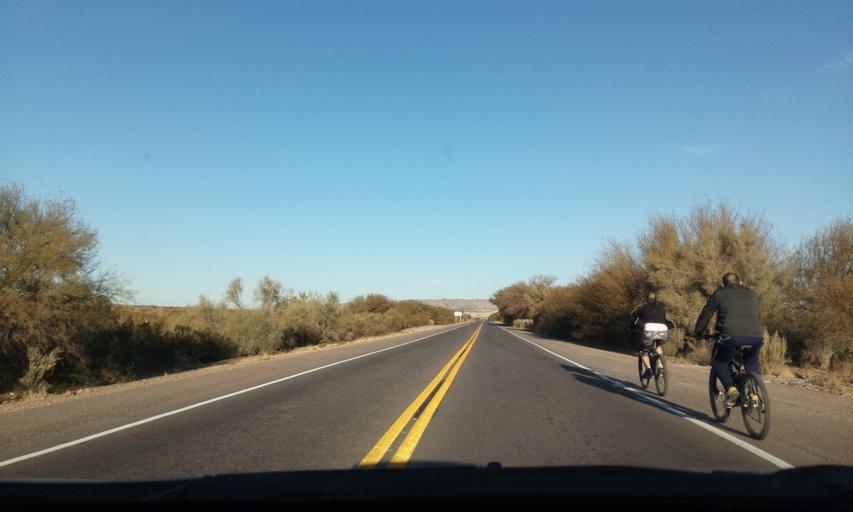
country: AR
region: San Juan
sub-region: Departamento de Rivadavia
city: Rivadavia
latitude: -31.4300
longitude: -68.6668
